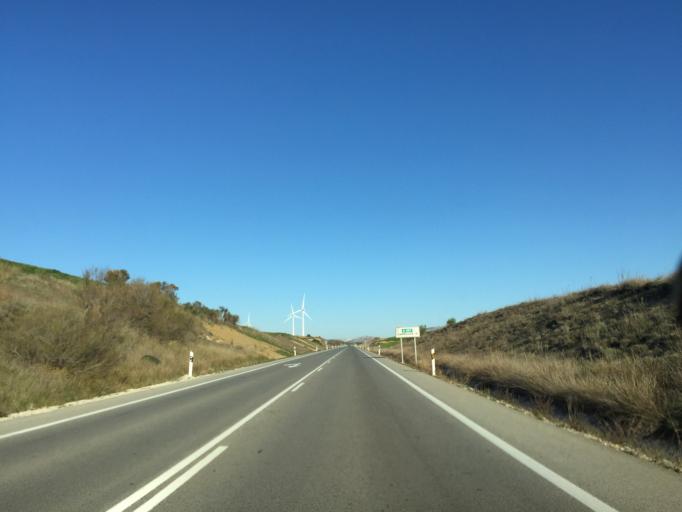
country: ES
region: Andalusia
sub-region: Provincia de Malaga
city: Ardales
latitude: 36.9237
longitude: -4.8469
